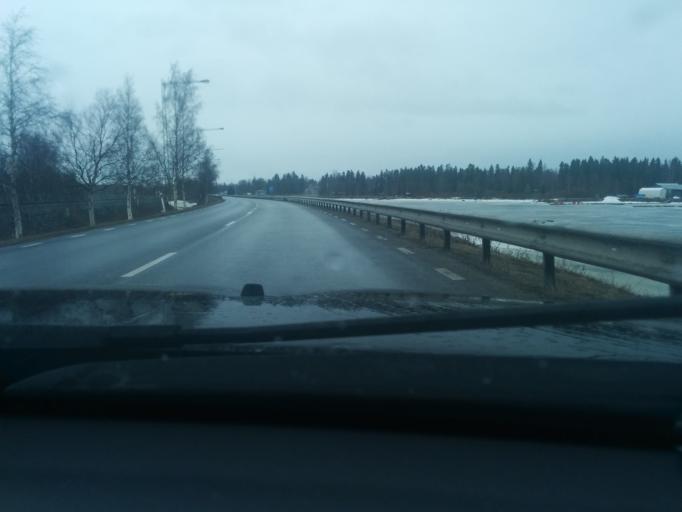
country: SE
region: Vaesterbotten
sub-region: Umea Kommun
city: Holmsund
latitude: 63.6954
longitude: 20.3559
